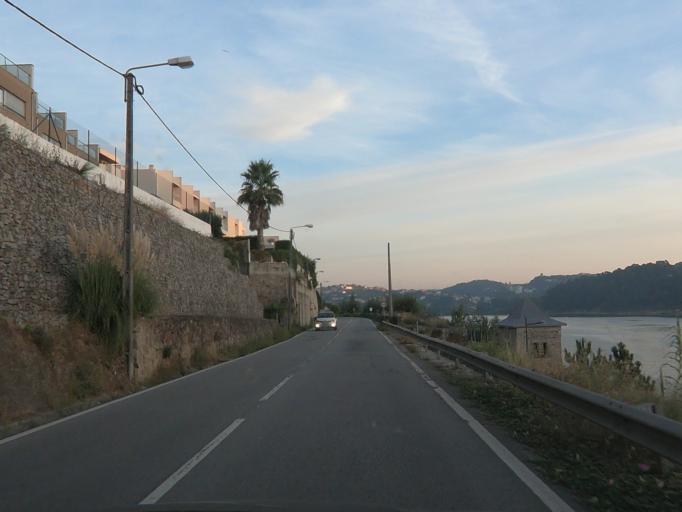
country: PT
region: Porto
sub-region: Gondomar
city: Valbom
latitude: 41.1358
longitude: -8.5708
